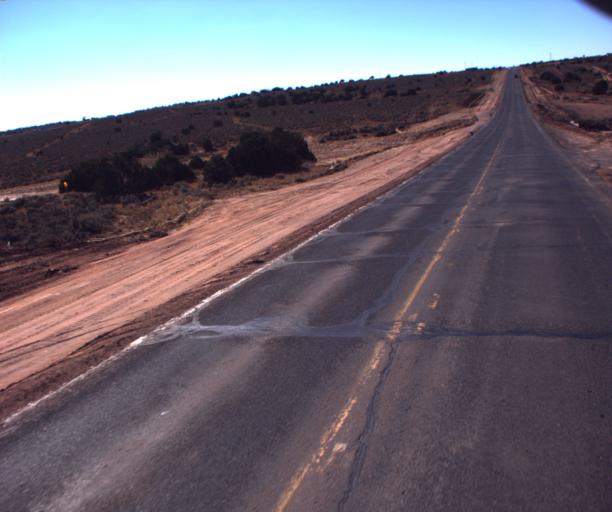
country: US
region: Arizona
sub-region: Apache County
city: Ganado
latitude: 35.7118
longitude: -109.4969
